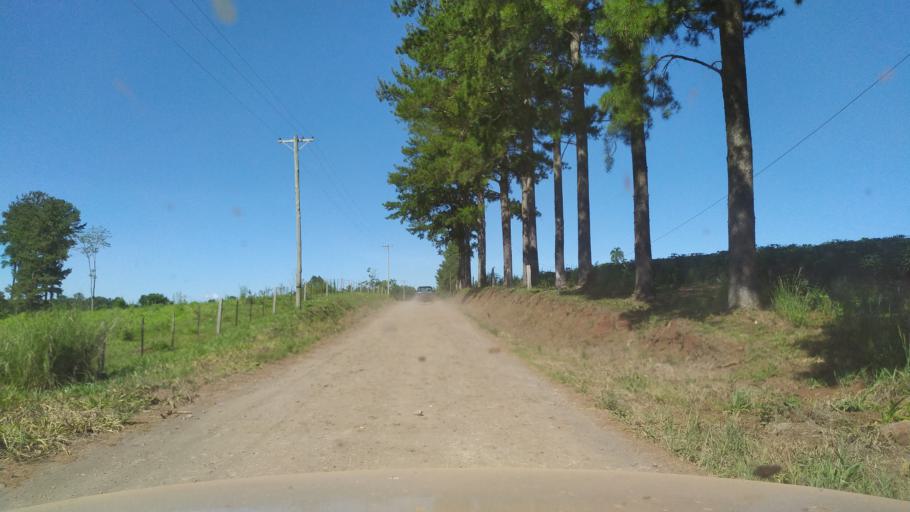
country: AR
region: Misiones
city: Caraguatay
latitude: -26.6796
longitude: -54.7059
